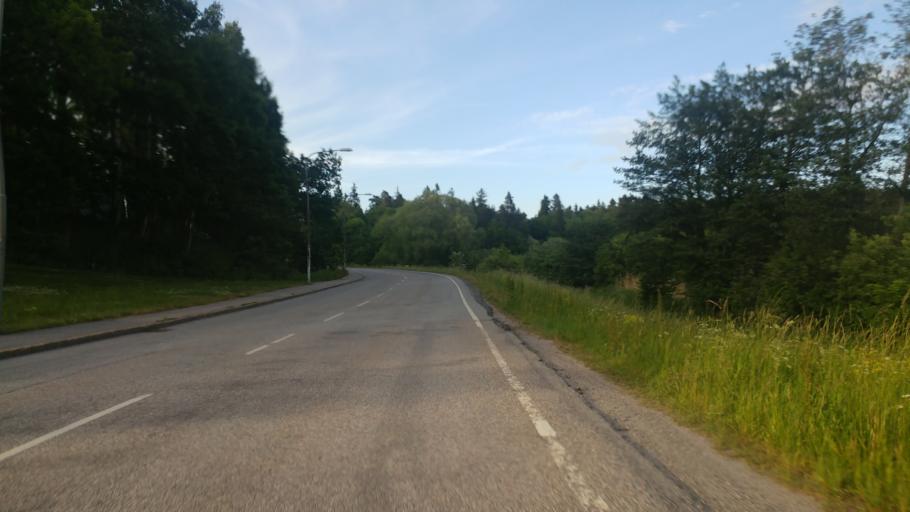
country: SE
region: Stockholm
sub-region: Danderyds Kommun
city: Djursholm
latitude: 59.3685
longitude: 18.0662
